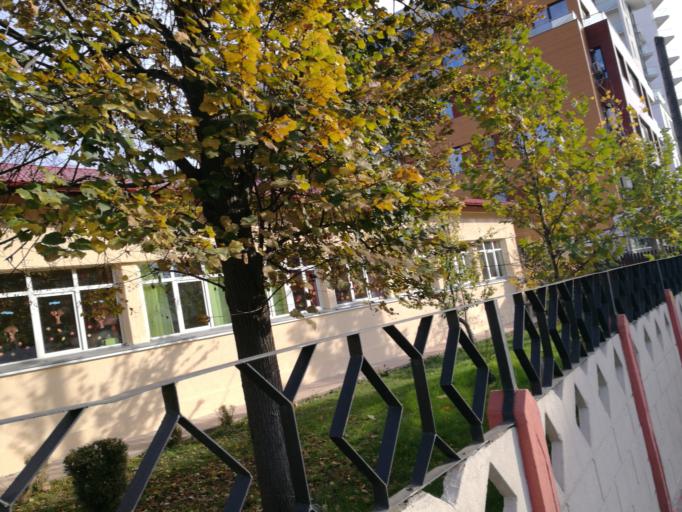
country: RO
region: Bucuresti
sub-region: Municipiul Bucuresti
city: Bucharest
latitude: 44.4780
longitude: 26.0926
